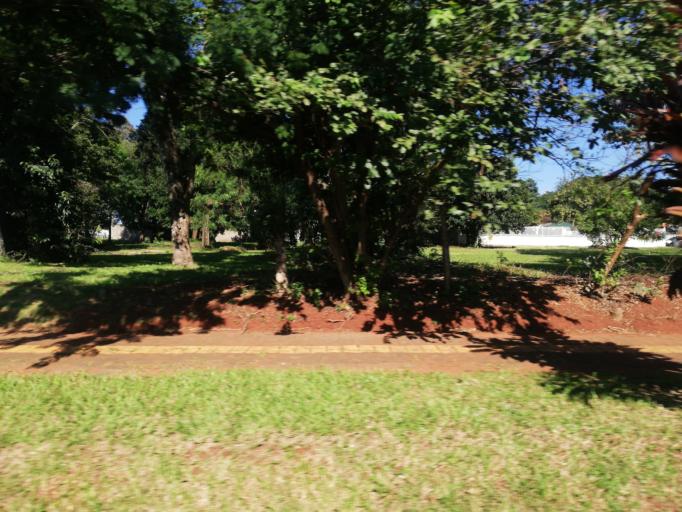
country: BR
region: Parana
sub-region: Foz Do Iguacu
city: Foz do Iguacu
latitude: -25.5547
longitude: -54.5672
